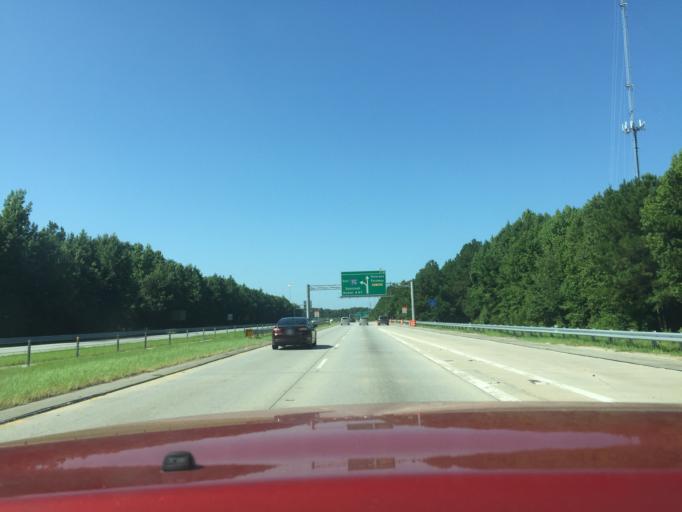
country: US
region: Georgia
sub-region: Chatham County
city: Savannah
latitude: 32.0501
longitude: -81.1435
